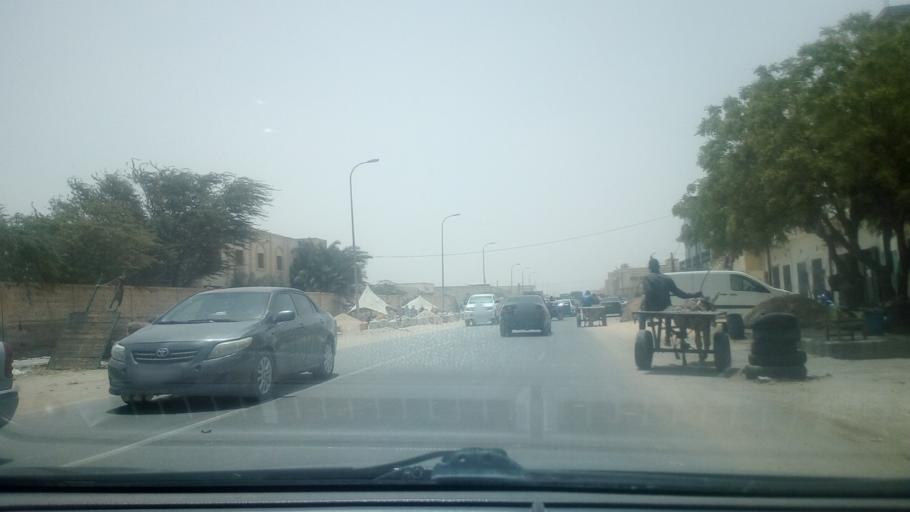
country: MR
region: Nouakchott
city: Nouakchott
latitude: 18.0757
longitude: -15.9849
